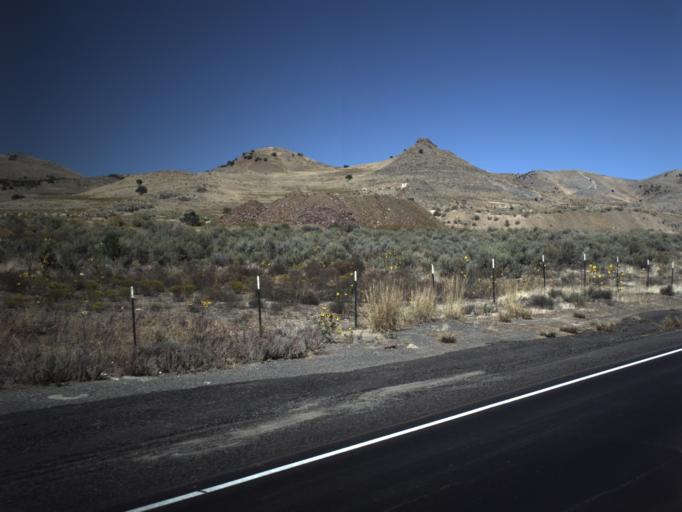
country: US
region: Utah
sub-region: Utah County
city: Saratoga Springs
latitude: 40.2130
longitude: -111.8887
